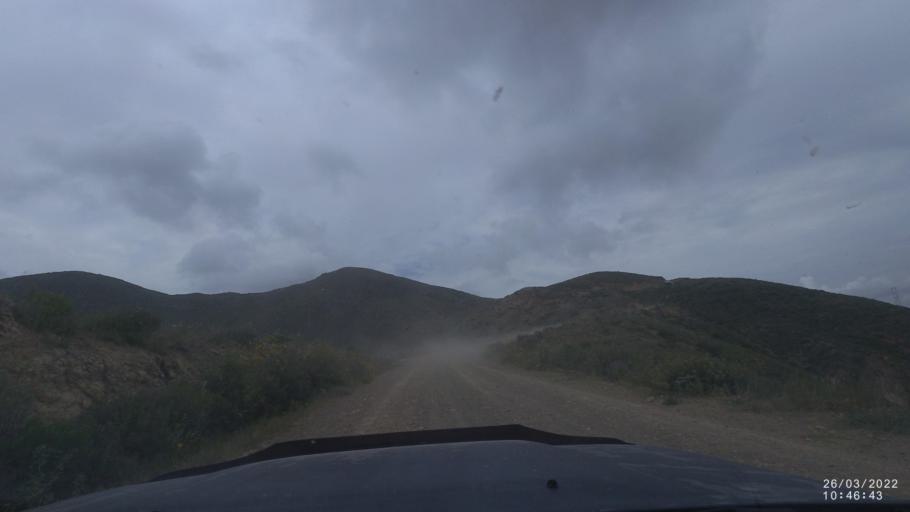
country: BO
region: Cochabamba
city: Tarata
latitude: -17.4887
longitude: -66.0488
